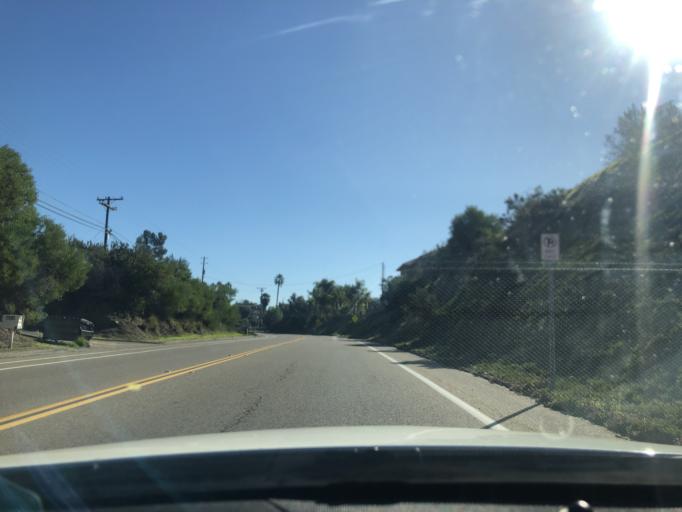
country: US
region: California
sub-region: San Diego County
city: Rancho San Diego
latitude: 32.7726
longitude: -116.9410
